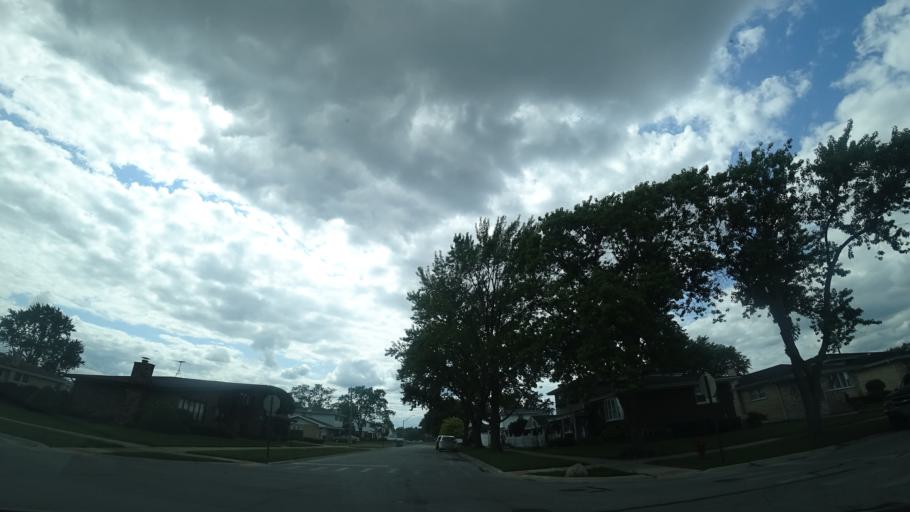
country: US
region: Illinois
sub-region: Cook County
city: Alsip
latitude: 41.6952
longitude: -87.7325
